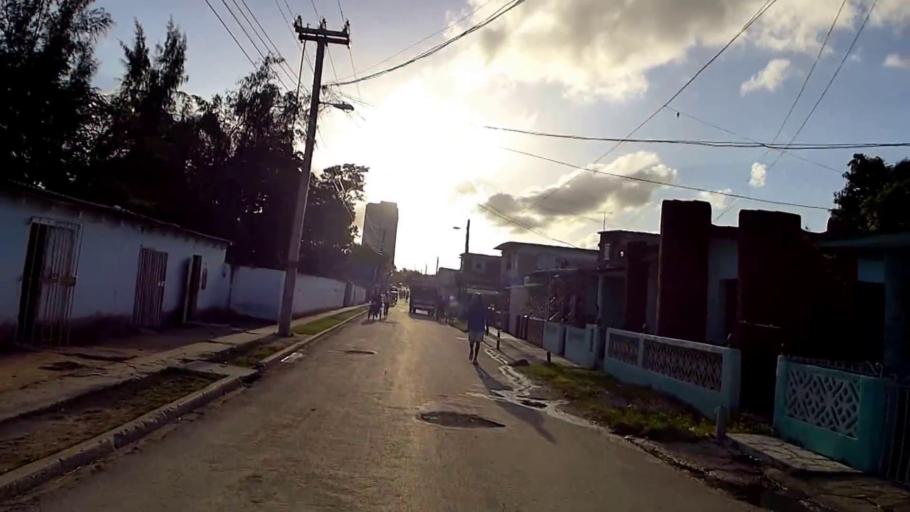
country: CU
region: Camaguey
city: Camaguey
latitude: 21.3948
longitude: -77.9052
